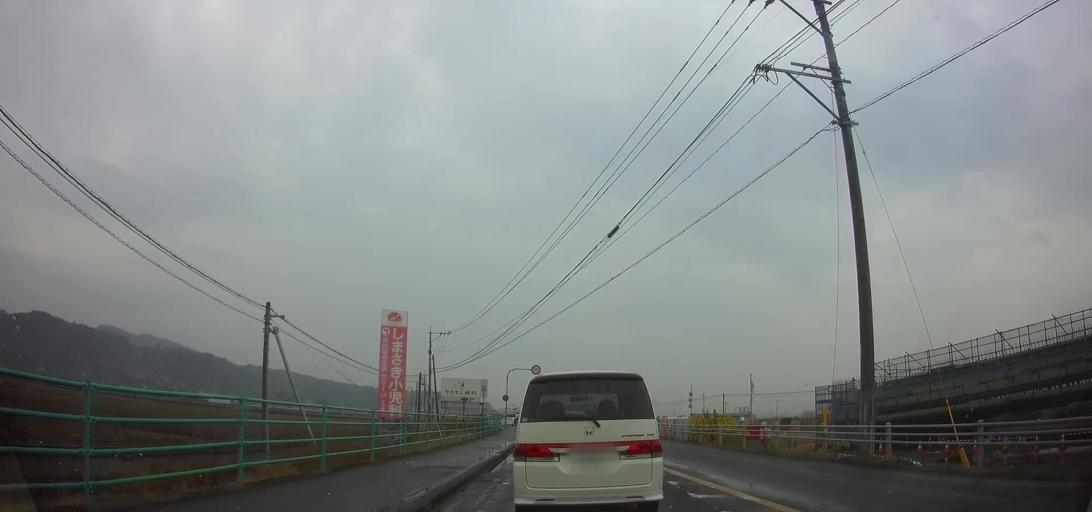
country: JP
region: Nagasaki
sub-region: Isahaya-shi
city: Isahaya
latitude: 32.8343
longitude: 130.1214
